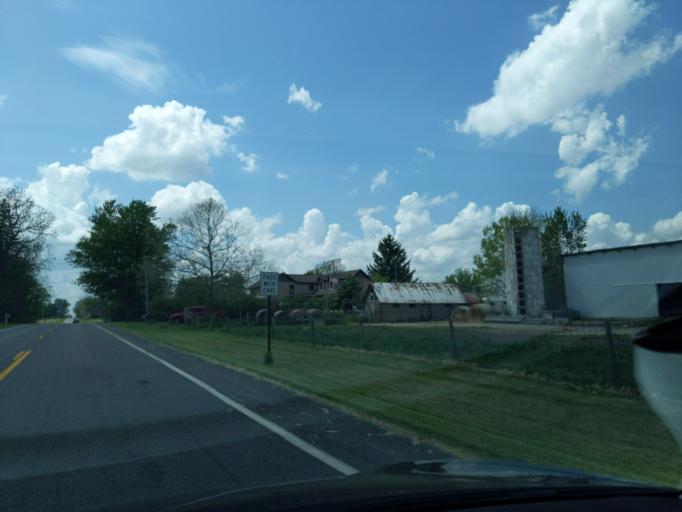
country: US
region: Michigan
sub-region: Ingham County
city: Mason
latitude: 42.5963
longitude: -84.3669
